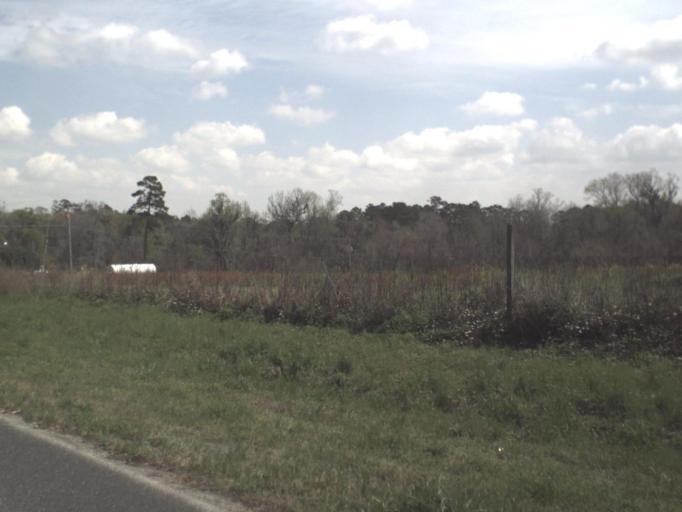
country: US
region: Florida
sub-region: Gadsden County
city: Havana
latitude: 30.6594
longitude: -84.4124
